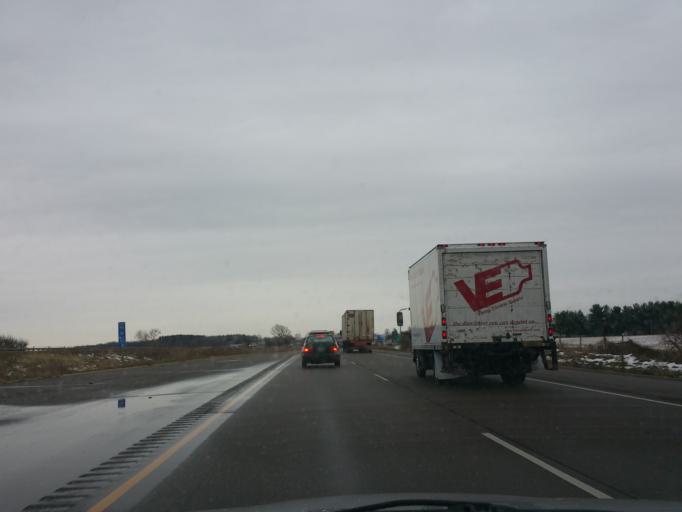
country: US
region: Wisconsin
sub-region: Rock County
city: Edgerton
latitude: 42.8543
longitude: -89.0363
